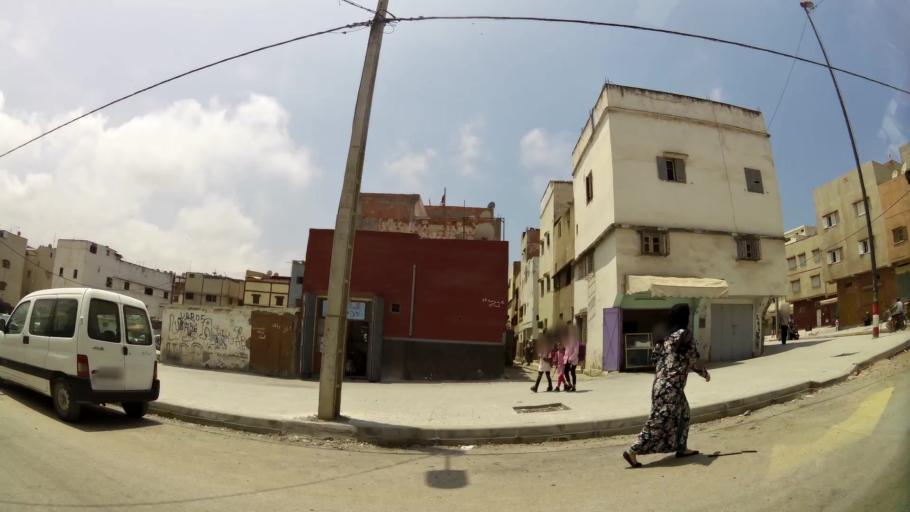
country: MA
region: Rabat-Sale-Zemmour-Zaer
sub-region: Rabat
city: Rabat
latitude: 33.9849
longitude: -6.8809
